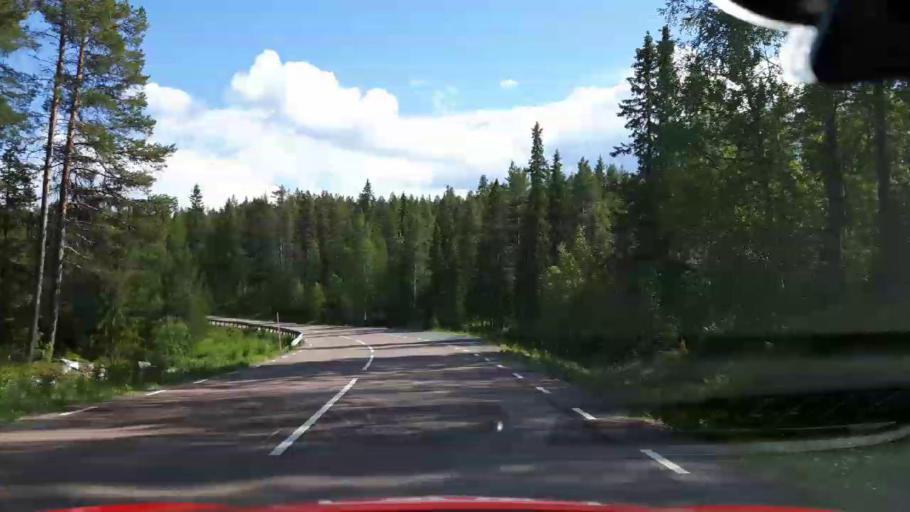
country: SE
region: Jaemtland
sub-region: Krokoms Kommun
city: Valla
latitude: 64.0096
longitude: 14.2320
